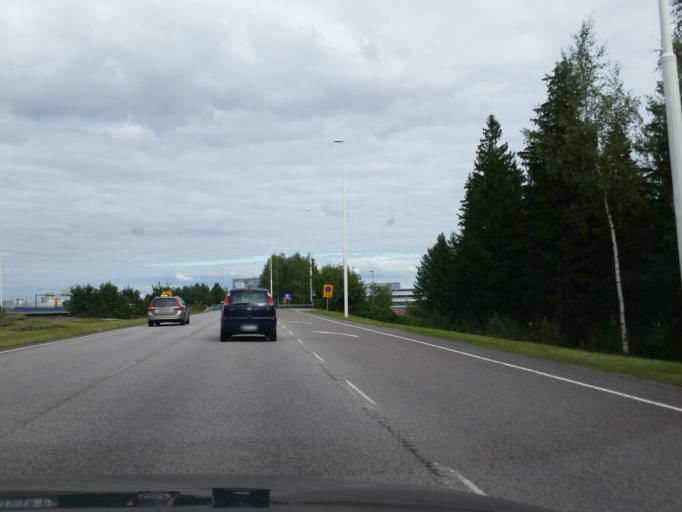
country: FI
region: Uusimaa
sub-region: Helsinki
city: Vantaa
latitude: 60.3095
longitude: 24.9686
